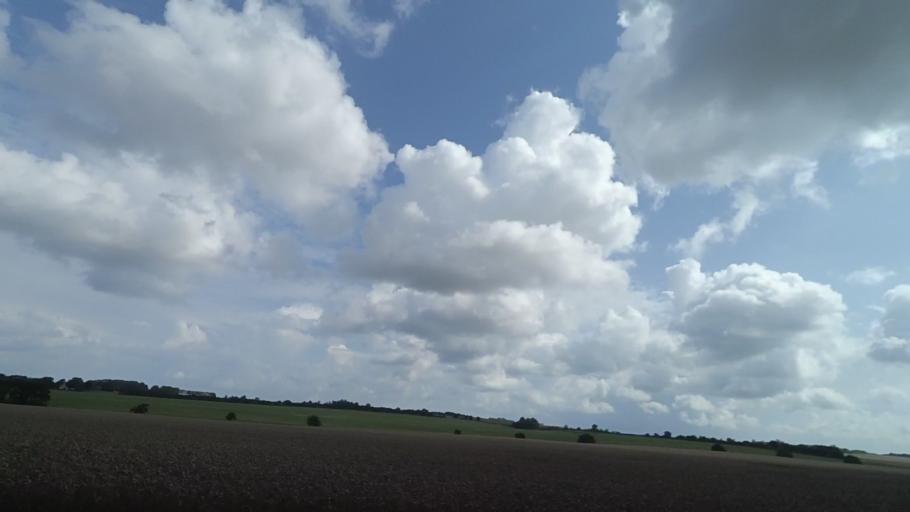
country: DK
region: Central Jutland
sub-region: Norddjurs Kommune
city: Auning
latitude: 56.4970
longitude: 10.4382
